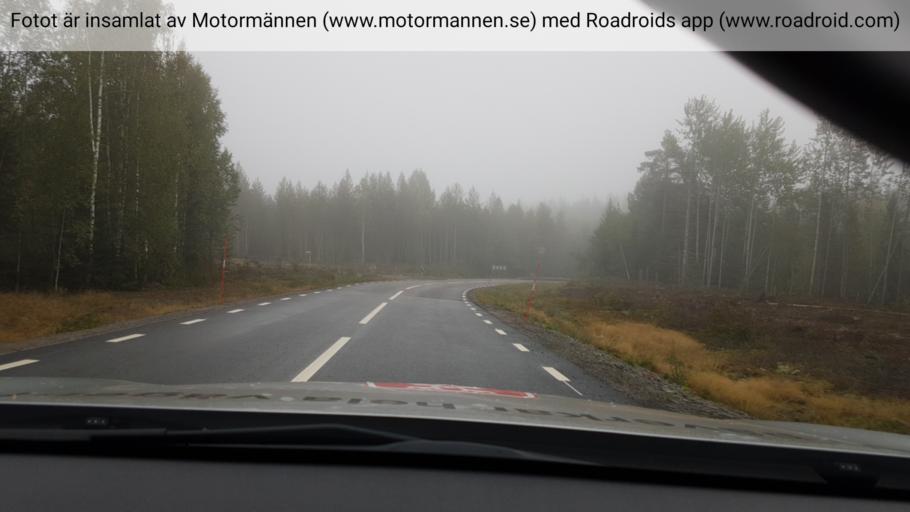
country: SE
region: Vaesterbotten
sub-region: Umea Kommun
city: Ersmark
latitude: 64.2628
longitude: 20.3428
